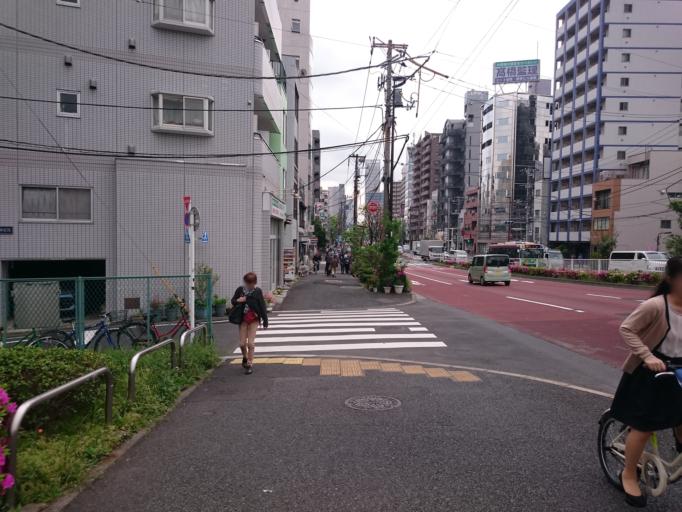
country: JP
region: Tokyo
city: Urayasu
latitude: 35.6713
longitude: 139.7940
